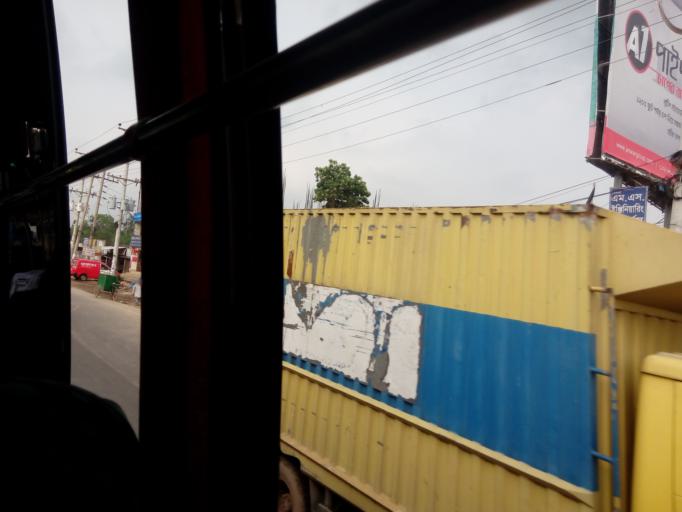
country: BD
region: Dhaka
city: Tungi
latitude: 23.9395
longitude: 90.2704
